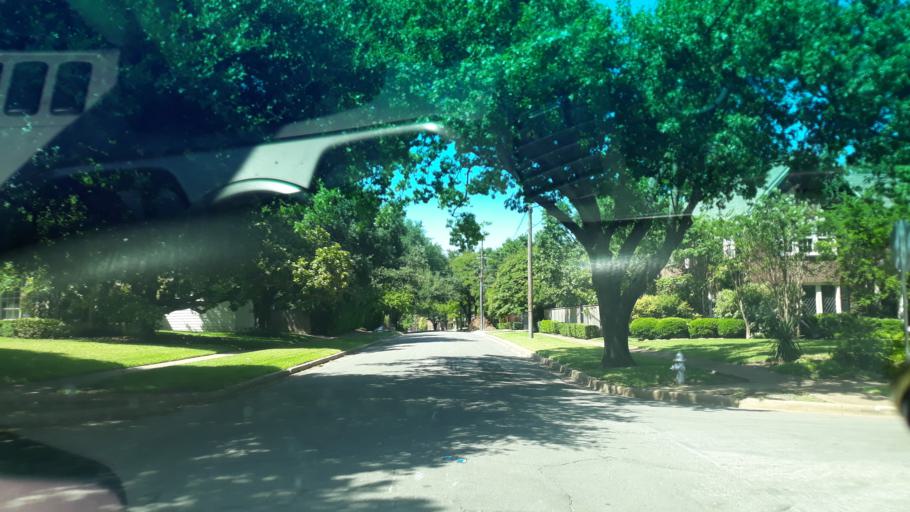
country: US
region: Texas
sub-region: Dallas County
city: Highland Park
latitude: 32.8177
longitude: -96.7465
